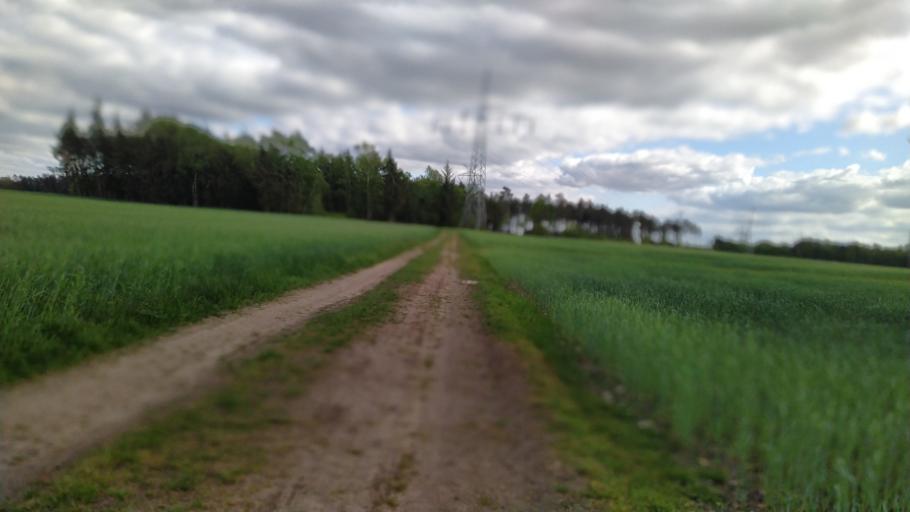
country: DE
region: Lower Saxony
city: Brest
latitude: 53.4372
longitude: 9.3933
